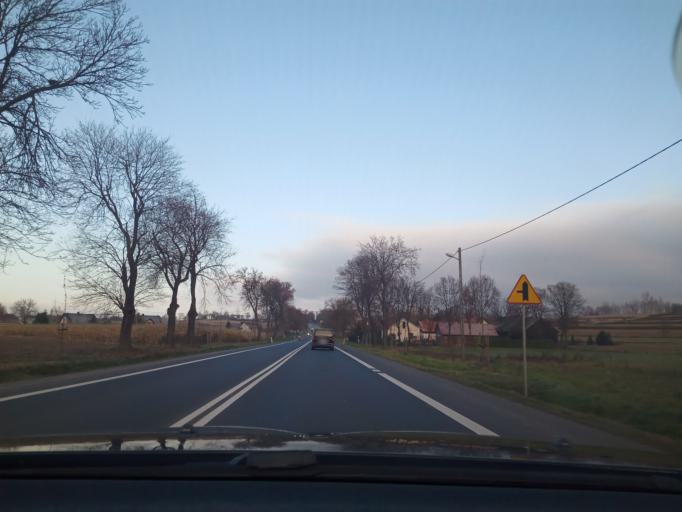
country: PL
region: Lesser Poland Voivodeship
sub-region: Powiat krakowski
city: Slomniki
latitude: 50.2855
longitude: 20.0533
